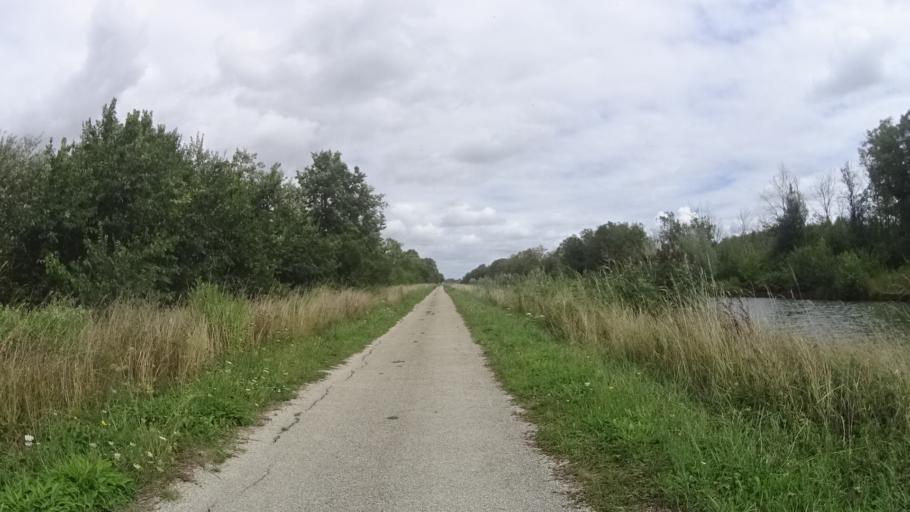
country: FR
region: Picardie
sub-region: Departement de l'Aisne
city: Ognes
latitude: 49.5973
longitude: 3.1999
